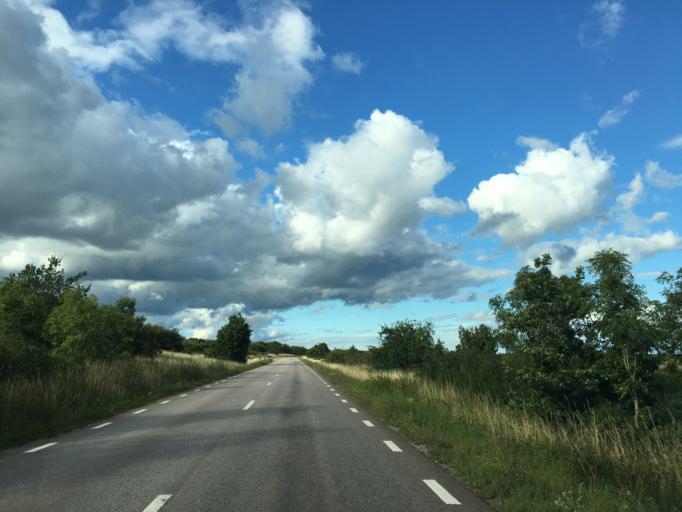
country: SE
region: Kalmar
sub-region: Morbylanga Kommun
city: Moerbylanga
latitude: 56.5561
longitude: 16.4457
